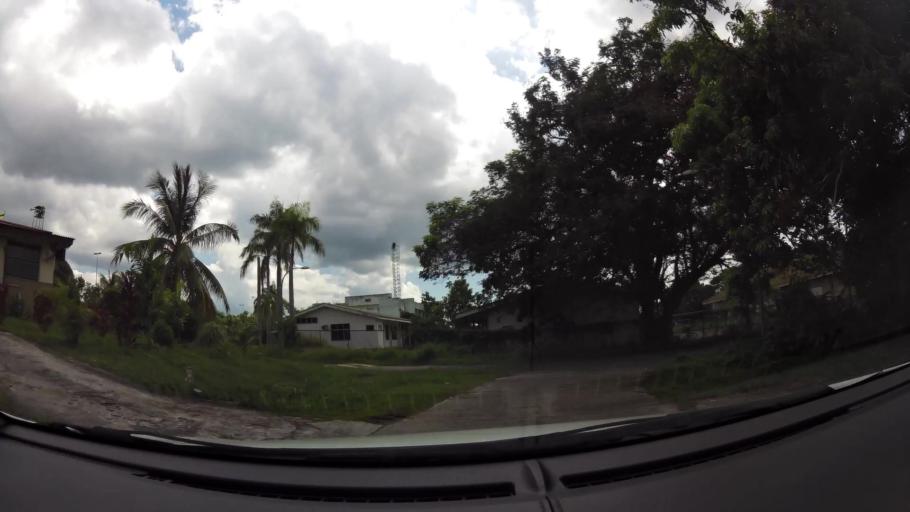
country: BN
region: Brunei and Muara
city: Bandar Seri Begawan
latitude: 4.9467
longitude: 114.9548
